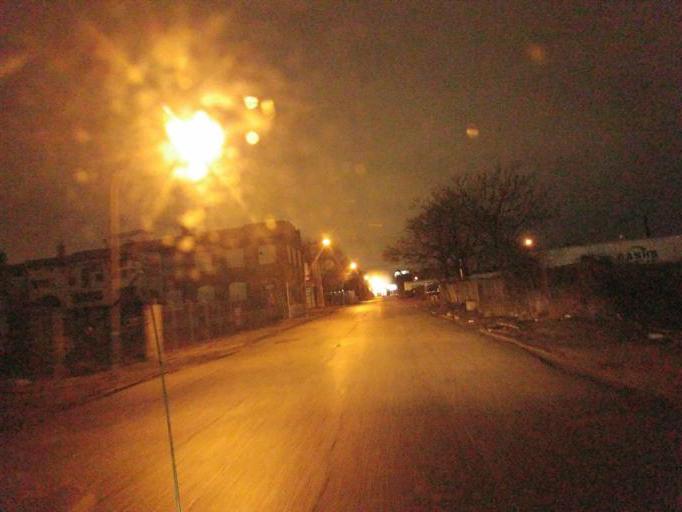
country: US
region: Illinois
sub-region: Madison County
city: Venice
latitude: 38.6561
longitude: -90.1937
